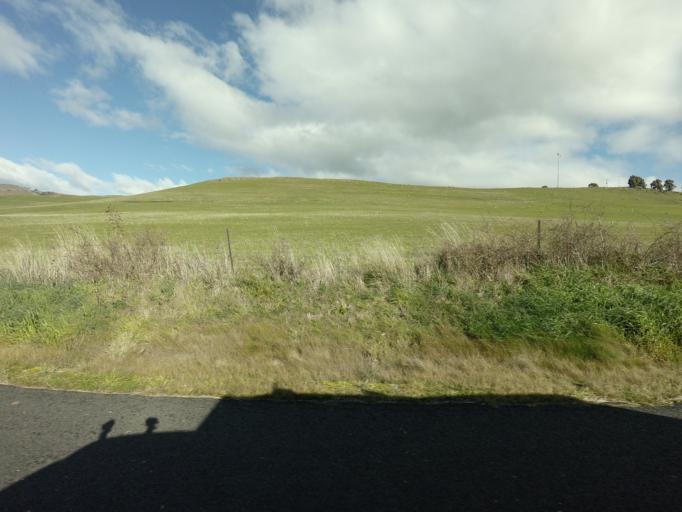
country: AU
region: Tasmania
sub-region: Derwent Valley
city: New Norfolk
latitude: -42.6933
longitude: 146.9489
